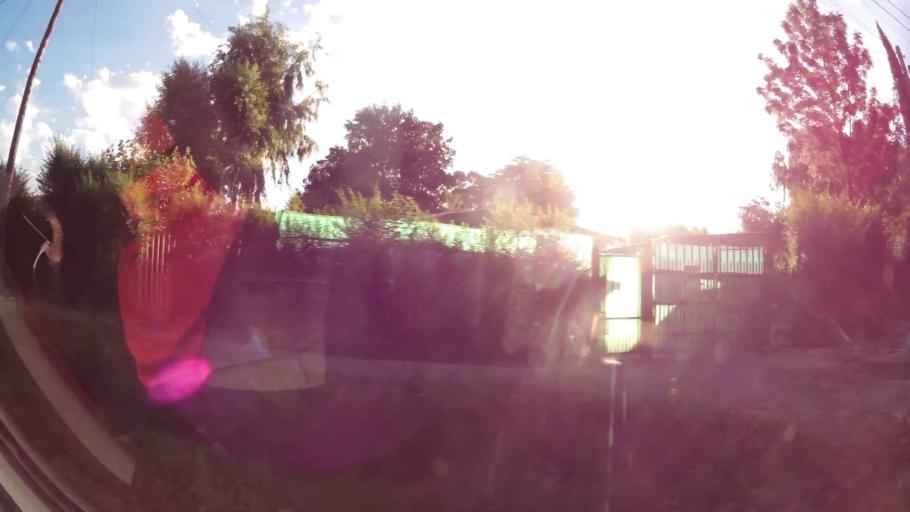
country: AR
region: Buenos Aires
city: Santa Catalina - Dique Lujan
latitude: -34.4691
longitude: -58.7461
